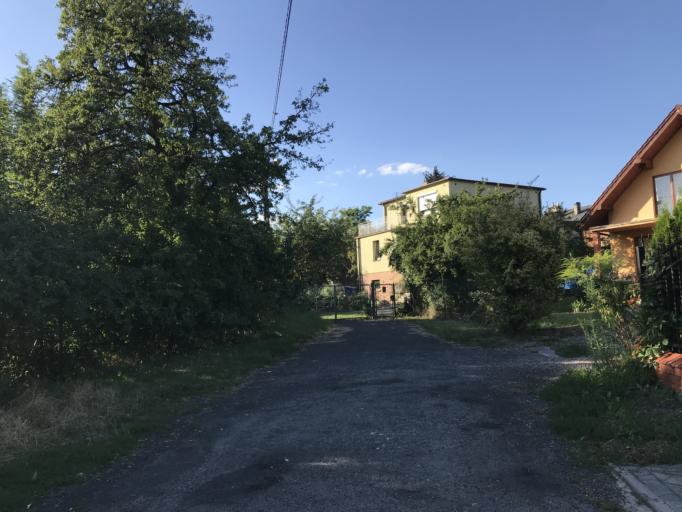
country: PL
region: Greater Poland Voivodeship
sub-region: Kalisz
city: Kalisz
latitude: 51.7673
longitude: 18.0998
